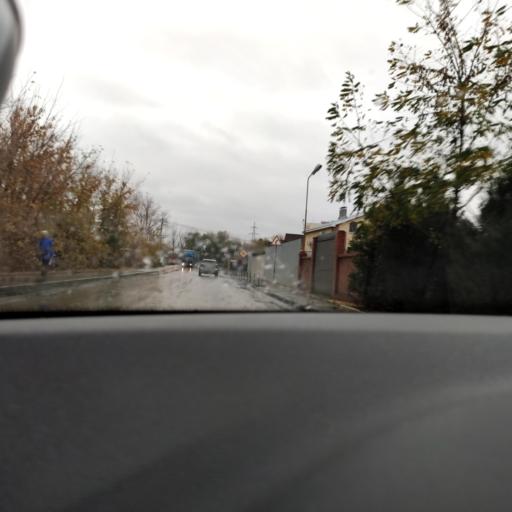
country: RU
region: Samara
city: Samara
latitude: 53.1577
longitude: 50.0832
